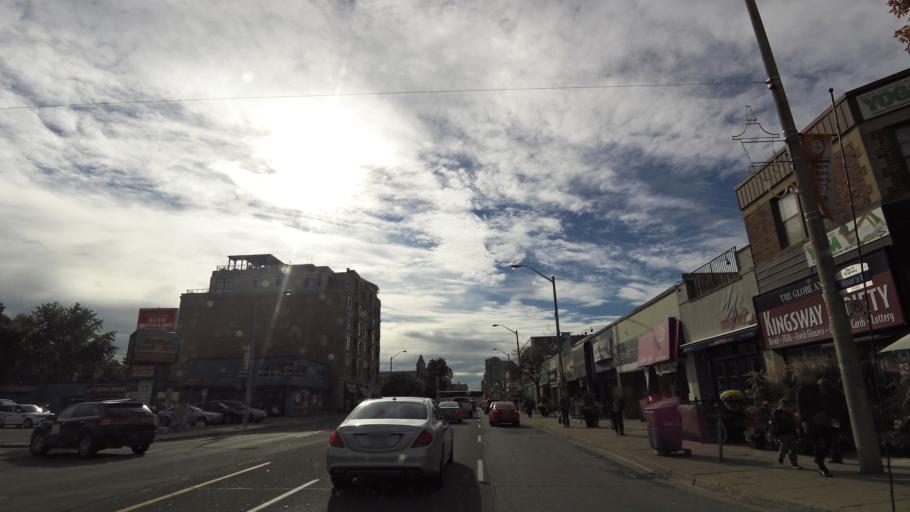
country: CA
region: Ontario
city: Etobicoke
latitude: 43.6477
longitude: -79.5101
